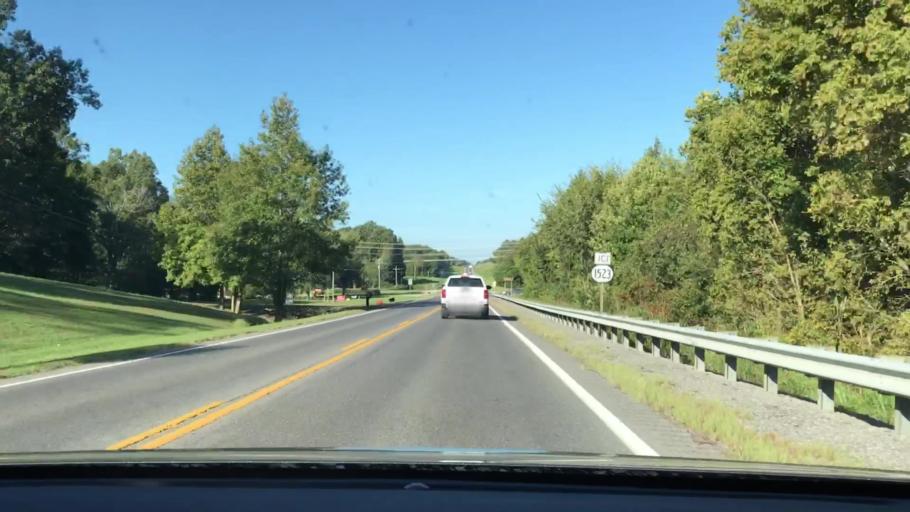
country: US
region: Kentucky
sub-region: Marshall County
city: Calvert City
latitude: 37.0049
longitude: -88.3879
